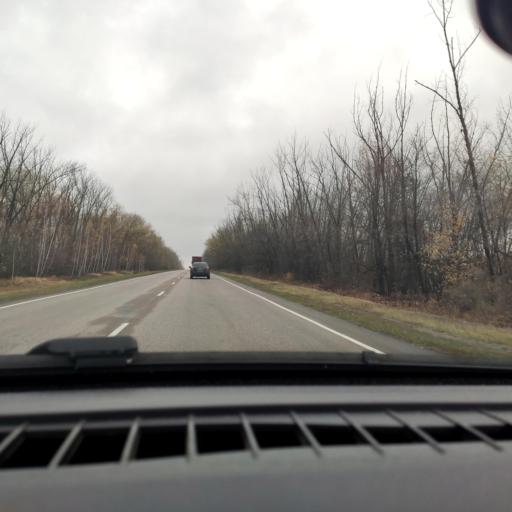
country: RU
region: Voronezj
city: Ostrogozhsk
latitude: 51.0102
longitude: 38.9945
